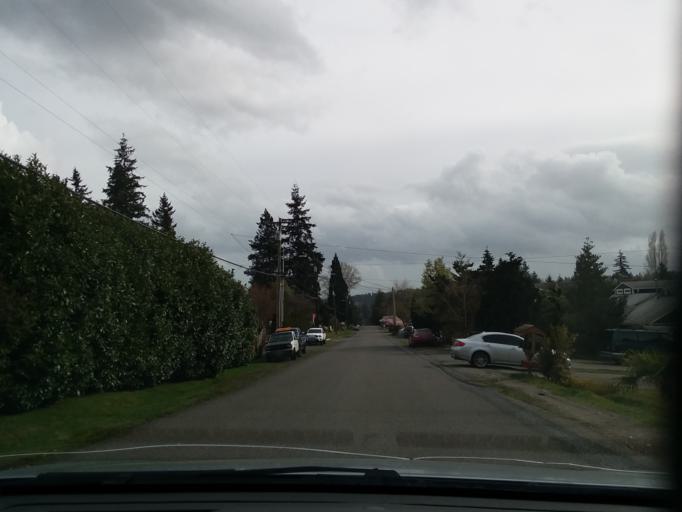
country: US
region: Washington
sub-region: Snohomish County
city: Mountlake Terrace
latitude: 47.7823
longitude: -122.3031
